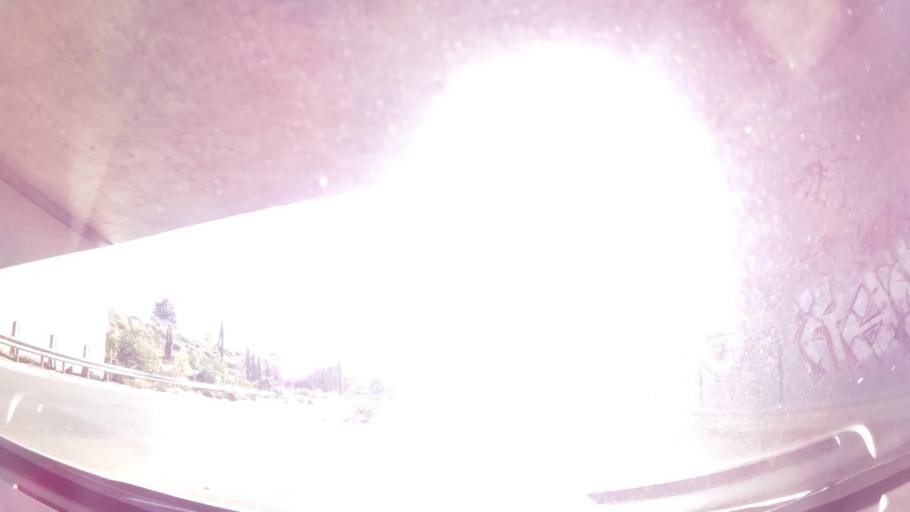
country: GR
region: Attica
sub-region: Nomarchia Athinas
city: Lykovrysi
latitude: 38.0959
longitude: 23.7748
